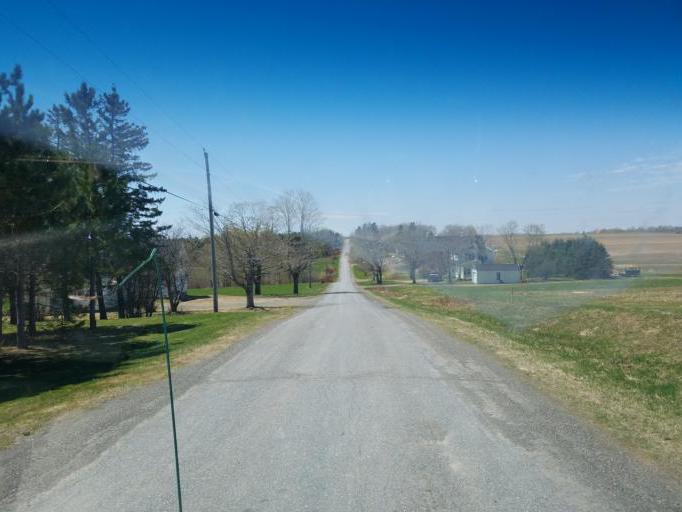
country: US
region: Maine
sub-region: Aroostook County
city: Caribou
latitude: 46.8673
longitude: -68.1976
